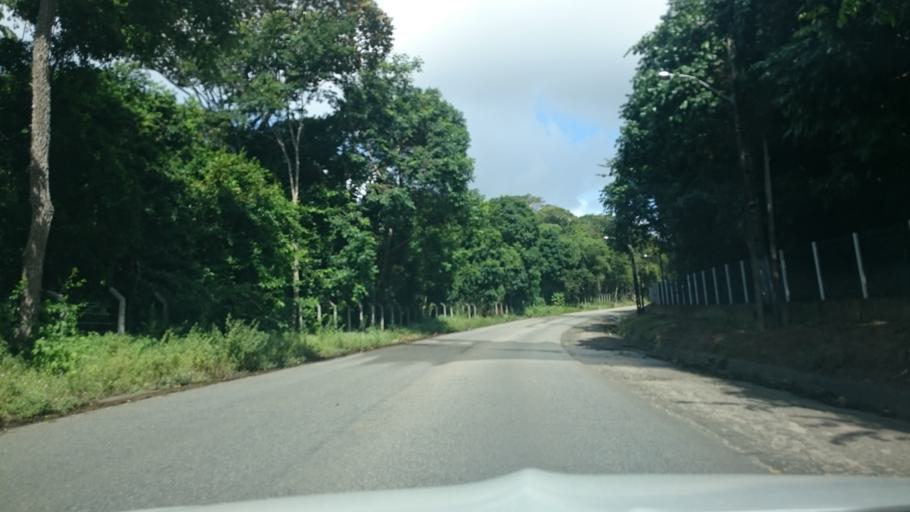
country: BR
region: Paraiba
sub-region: Joao Pessoa
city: Joao Pessoa
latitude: -7.1396
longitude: -34.8430
